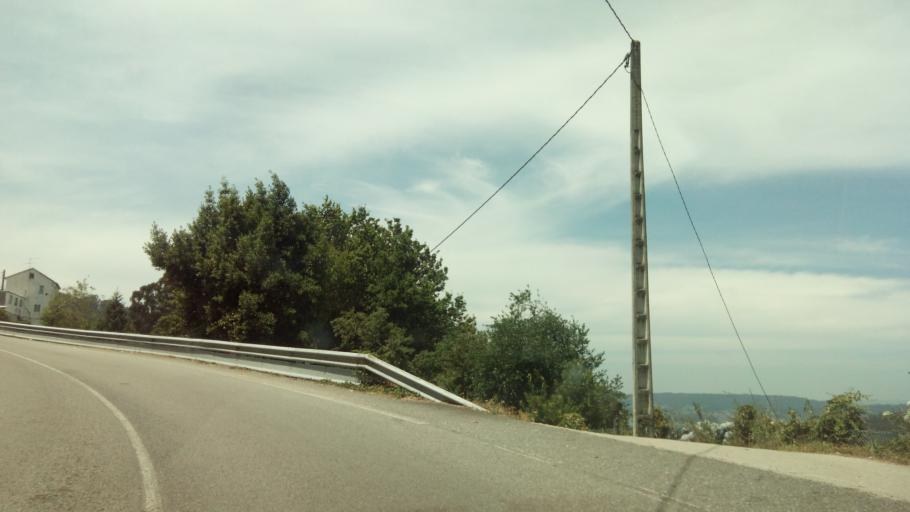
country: ES
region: Galicia
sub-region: Provincia de Pontevedra
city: Marin
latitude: 42.3493
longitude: -8.6989
